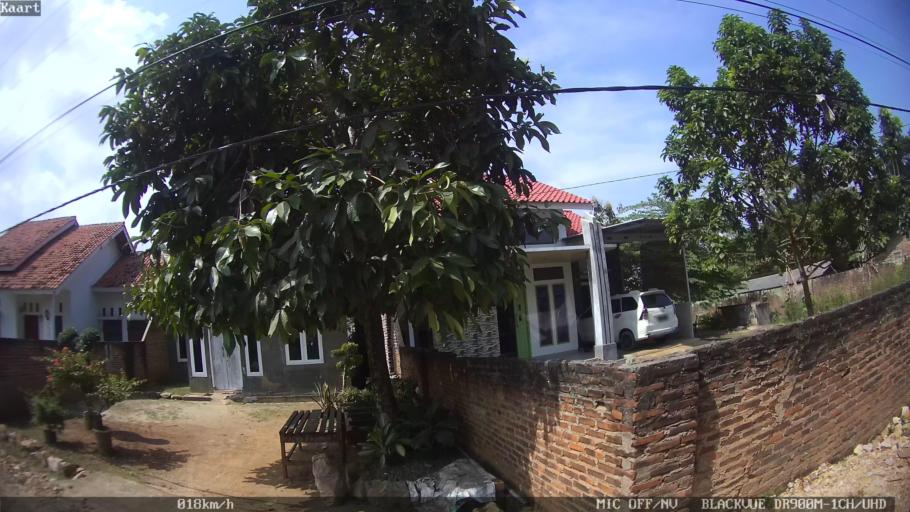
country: ID
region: Lampung
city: Kedaton
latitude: -5.3293
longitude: 105.2774
